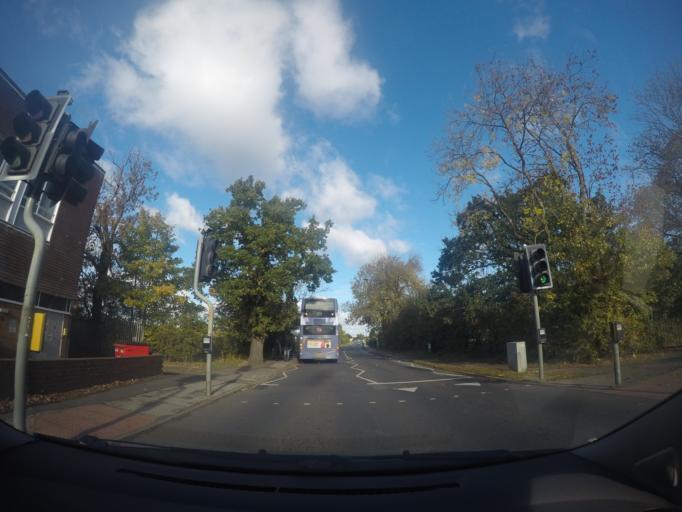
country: GB
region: England
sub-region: City of York
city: Haxby
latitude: 53.9981
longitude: -1.0723
